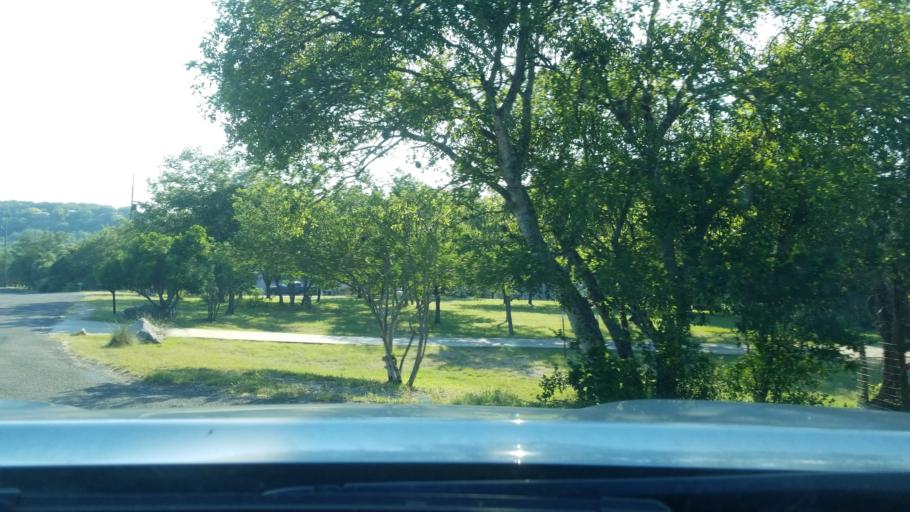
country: US
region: Texas
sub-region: Comal County
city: Bulverde
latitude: 29.7132
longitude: -98.4304
